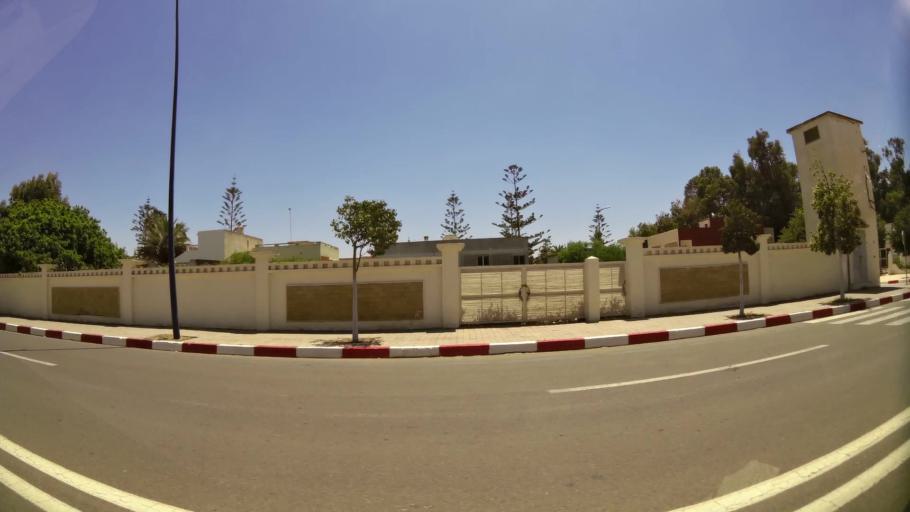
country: MA
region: Oriental
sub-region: Berkane-Taourirt
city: Madagh
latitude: 35.0874
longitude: -2.2343
